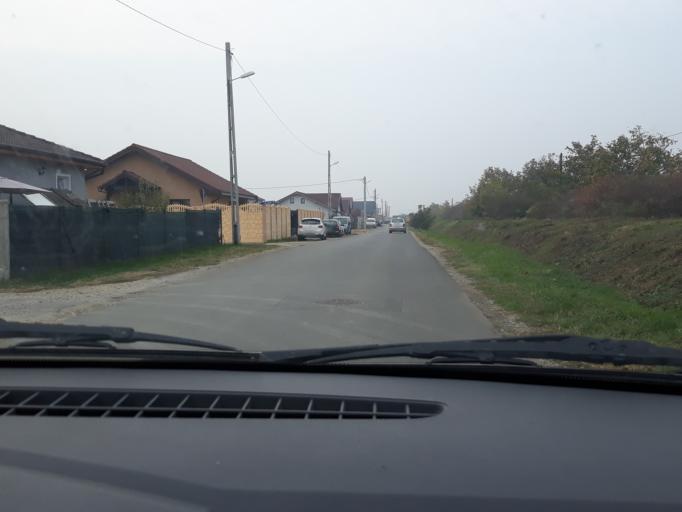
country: RO
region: Bihor
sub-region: Comuna Santandrei
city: Santandrei
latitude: 47.0628
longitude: 21.8564
